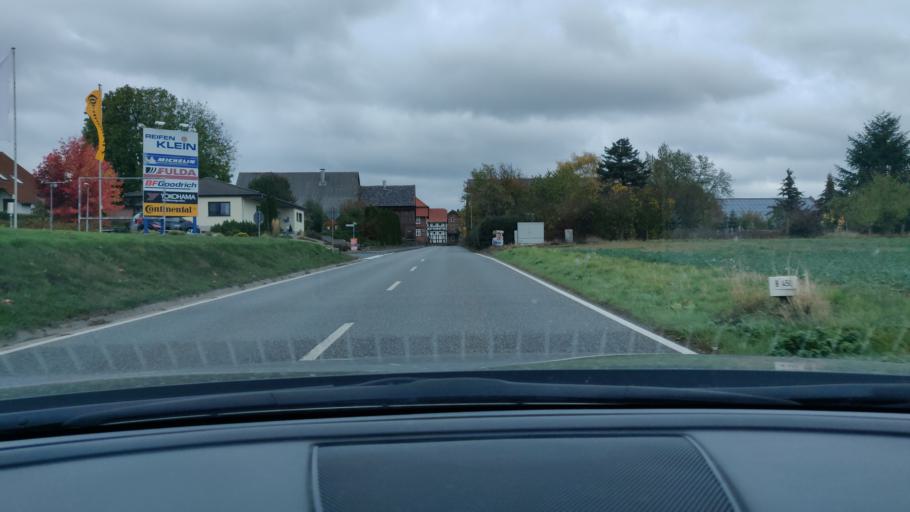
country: DE
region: Hesse
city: Fritzlar
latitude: 51.1772
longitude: 9.2671
